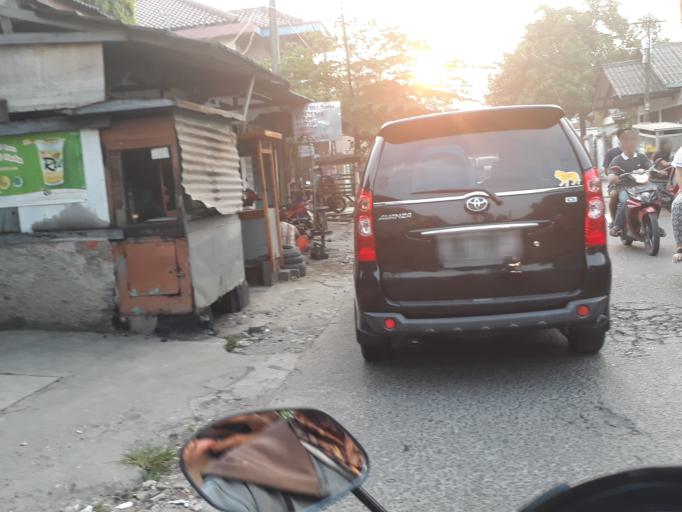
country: ID
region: West Java
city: Bekasi
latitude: -6.2397
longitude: 107.0365
